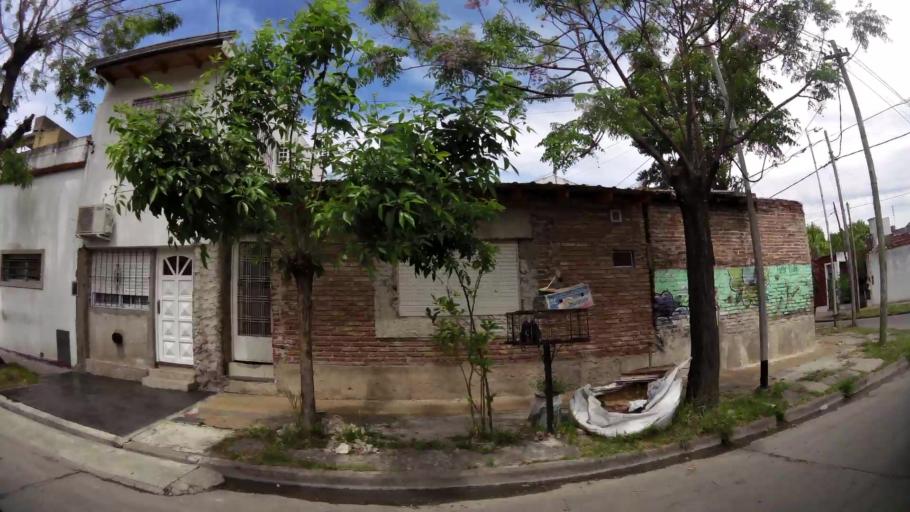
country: AR
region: Buenos Aires
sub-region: Partido de Avellaneda
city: Avellaneda
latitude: -34.6646
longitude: -58.4032
